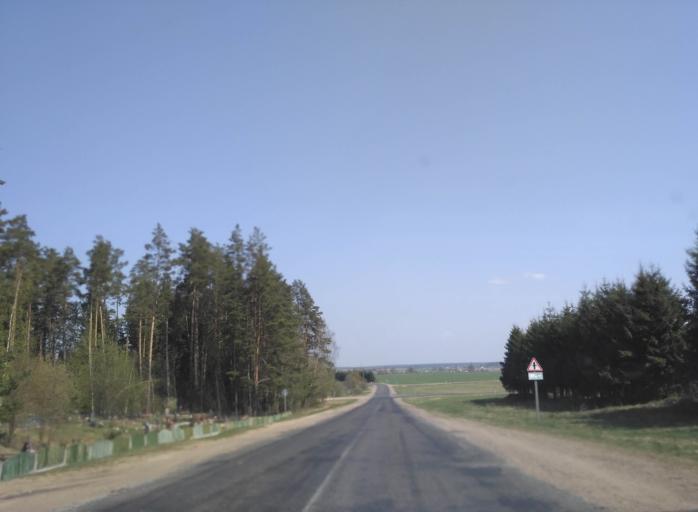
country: BY
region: Minsk
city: Horad Barysaw
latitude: 54.2893
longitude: 28.5261
